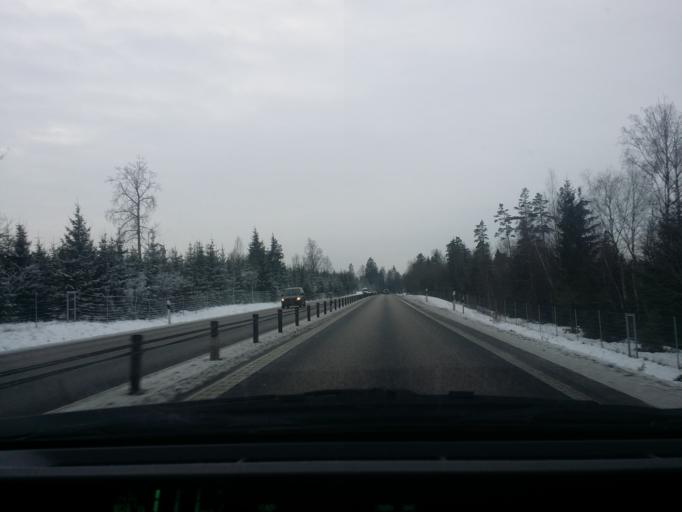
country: SE
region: Vaestra Goetaland
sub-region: Toreboda Kommun
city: Toereboda
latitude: 58.7835
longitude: 14.0118
